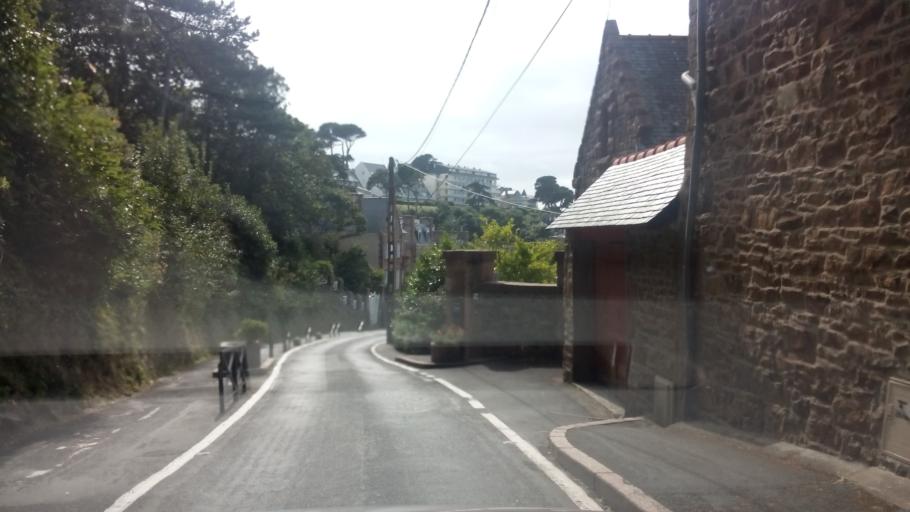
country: FR
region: Brittany
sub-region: Departement des Cotes-d'Armor
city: Perros-Guirec
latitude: 48.8158
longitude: -3.4495
